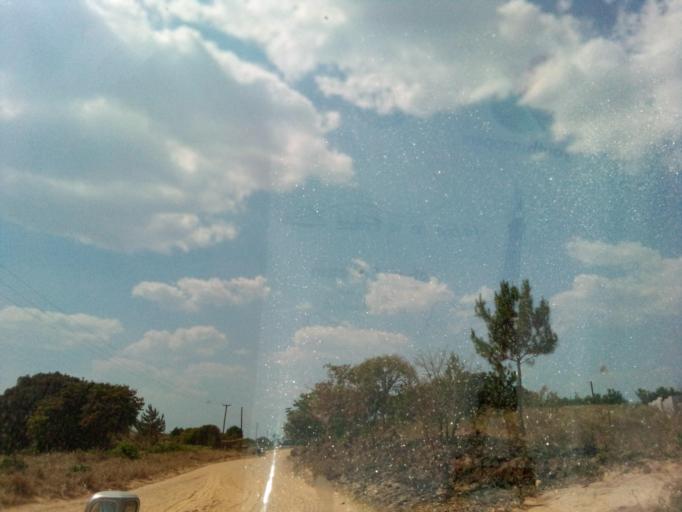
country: ZM
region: Northern
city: Mpika
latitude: -11.8415
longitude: 31.3850
